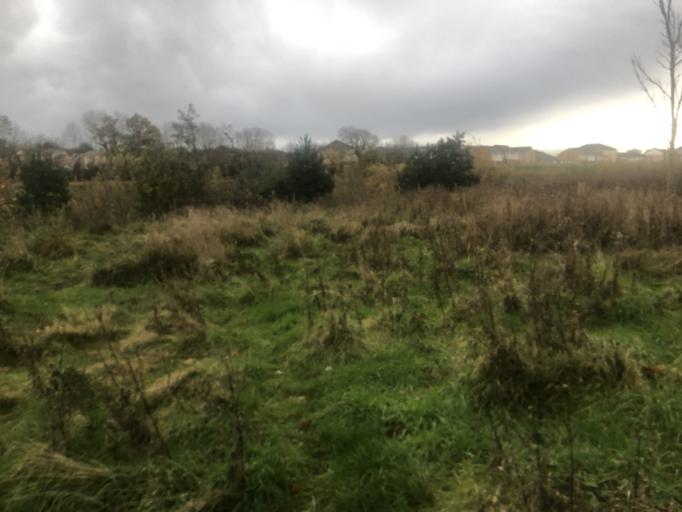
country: GB
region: Scotland
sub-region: West Lothian
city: Seafield
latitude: 55.9283
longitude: -3.1201
